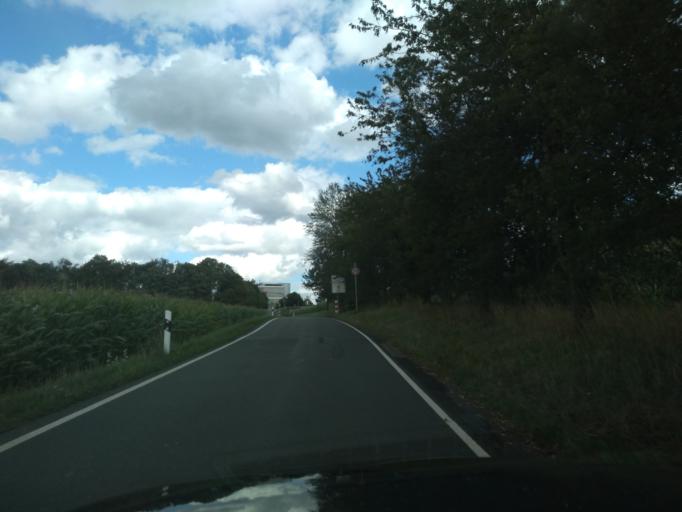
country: DE
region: North Rhine-Westphalia
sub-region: Regierungsbezirk Arnsberg
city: Luedenscheid
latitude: 51.2382
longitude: 7.6042
